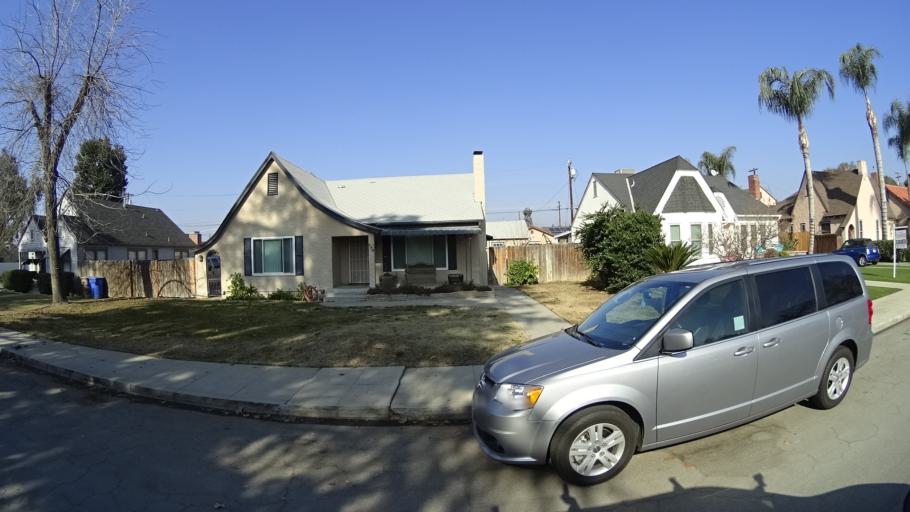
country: US
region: California
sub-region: Kern County
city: Bakersfield
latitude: 35.3893
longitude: -118.9968
